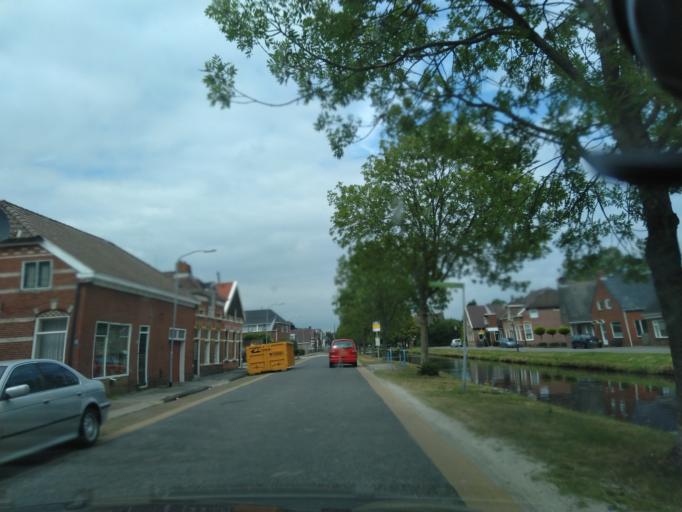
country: NL
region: Groningen
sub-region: Gemeente Pekela
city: Oude Pekela
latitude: 53.0939
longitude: 6.9893
